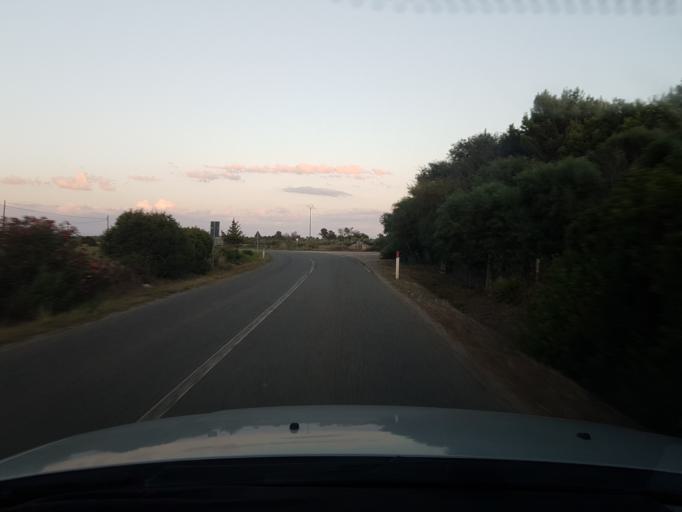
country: IT
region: Sardinia
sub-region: Provincia di Oristano
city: Riola Sardo
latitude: 40.0256
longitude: 8.4303
